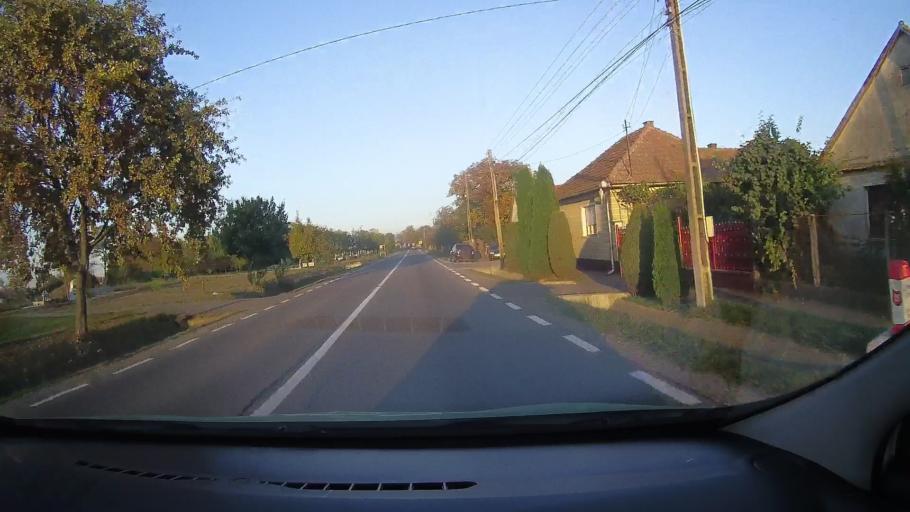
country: RO
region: Bihor
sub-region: Comuna Rosiori
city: Rosiori
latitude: 47.2601
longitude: 21.9623
